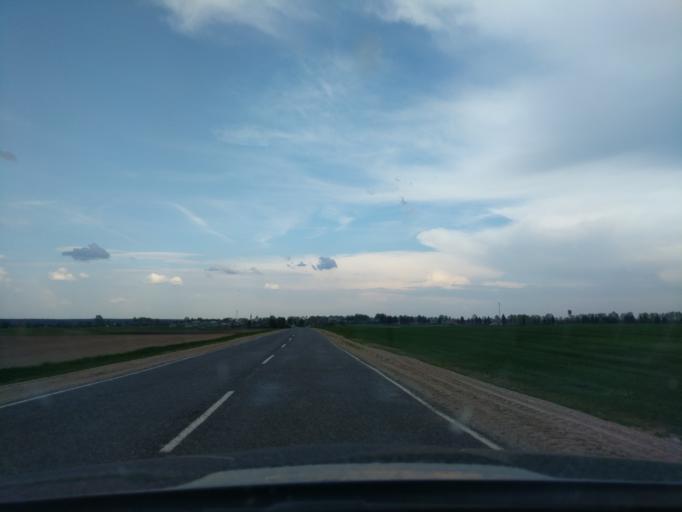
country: BY
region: Grodnenskaya
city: Lyubcha
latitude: 53.7519
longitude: 26.0351
